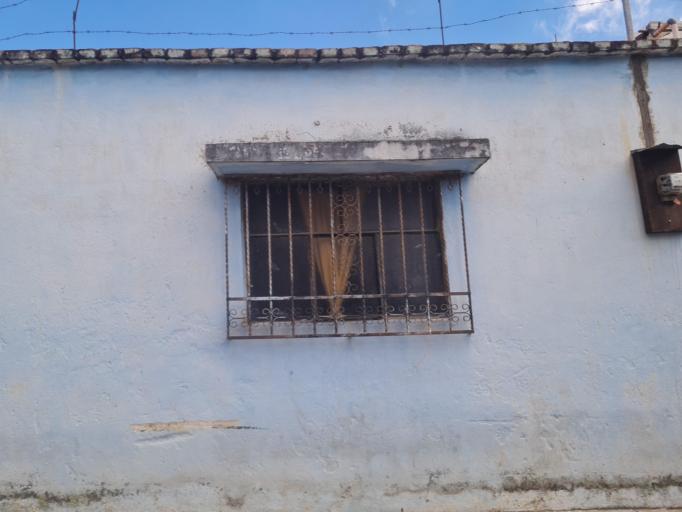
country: GT
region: Quetzaltenango
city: Quetzaltenango
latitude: 14.8373
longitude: -91.5327
